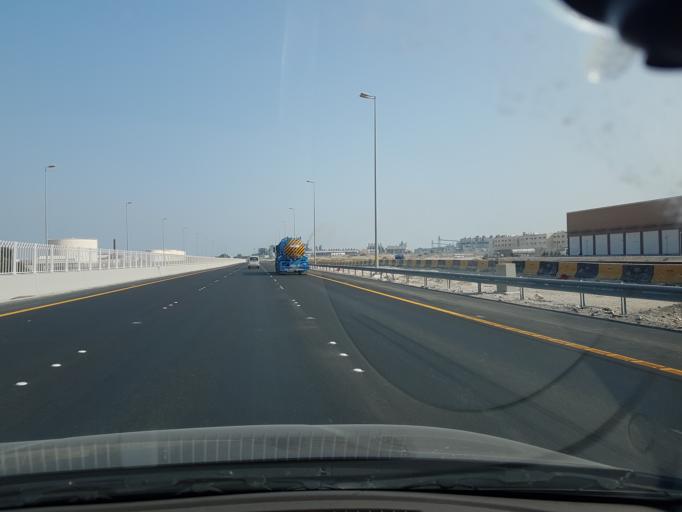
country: BH
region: Northern
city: Ar Rifa'
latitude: 26.1066
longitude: 50.6001
